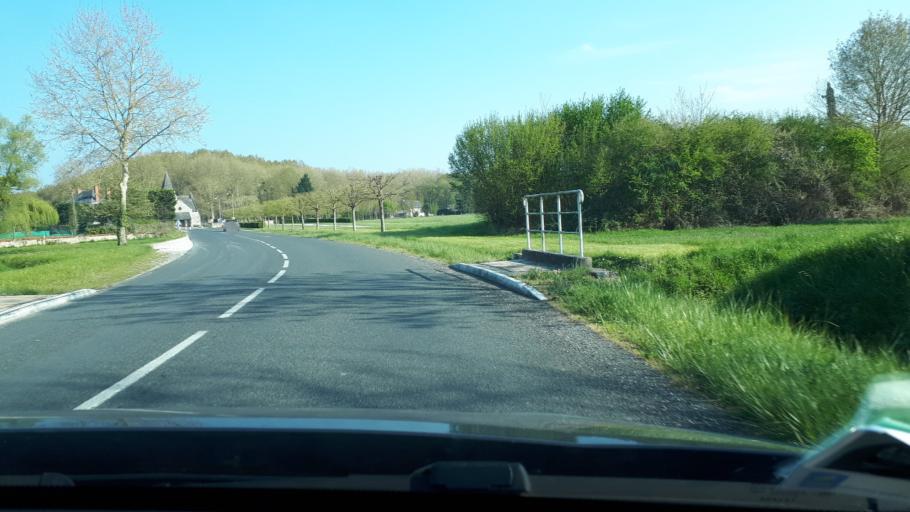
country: FR
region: Centre
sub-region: Departement d'Indre-et-Loire
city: La Croix-en-Touraine
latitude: 47.3366
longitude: 0.9875
